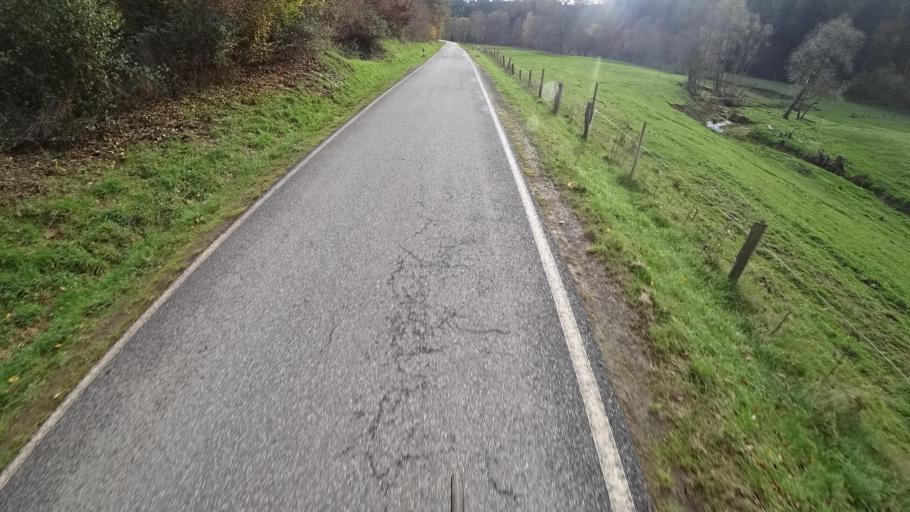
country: DE
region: Rheinland-Pfalz
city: Sierscheid
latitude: 50.4794
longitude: 6.9160
